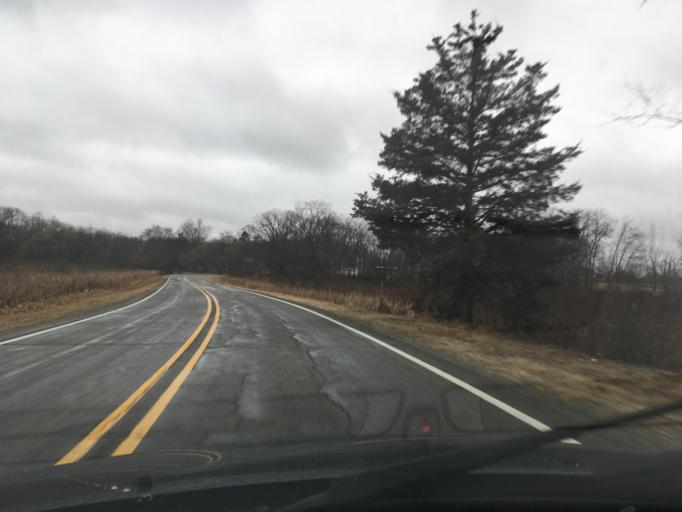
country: US
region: Michigan
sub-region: Washtenaw County
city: Chelsea
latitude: 42.3110
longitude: -84.1090
